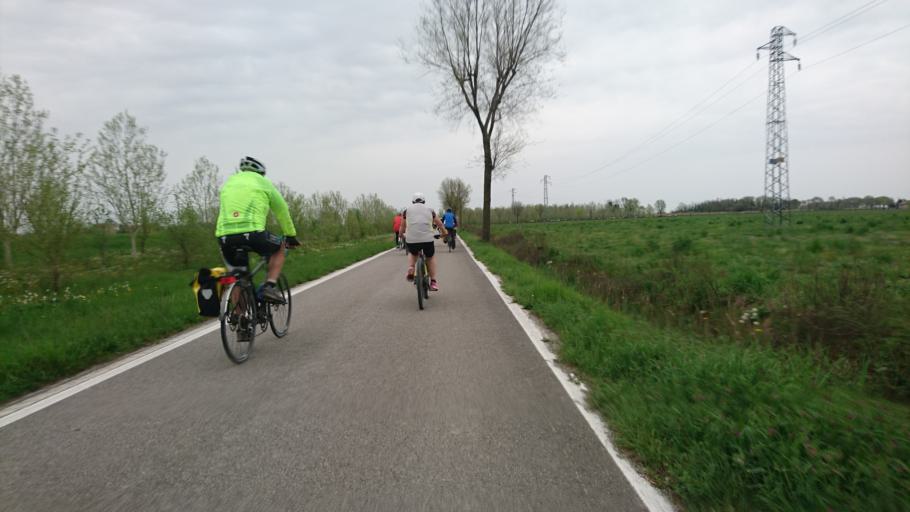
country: IT
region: Veneto
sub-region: Provincia di Venezia
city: Cesarolo
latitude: 45.6867
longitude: 12.9886
